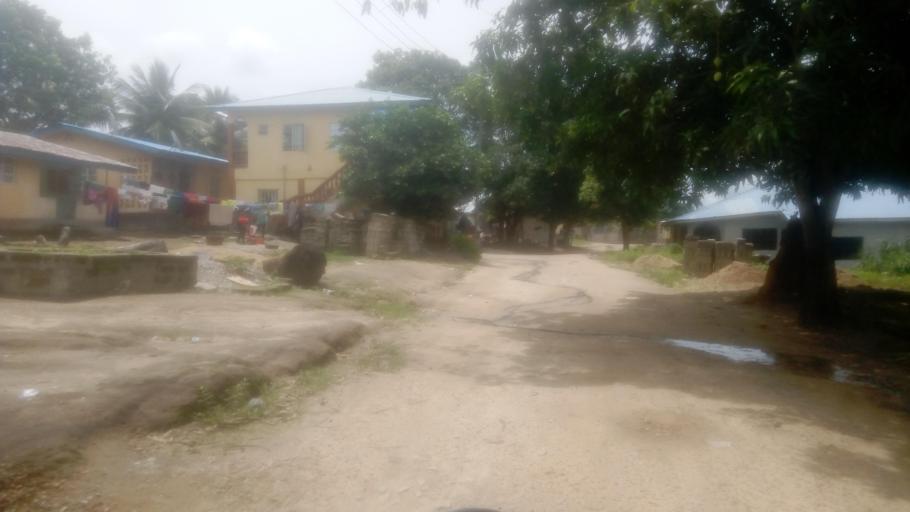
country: SL
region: Southern Province
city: Bo
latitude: 7.9512
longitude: -11.7129
